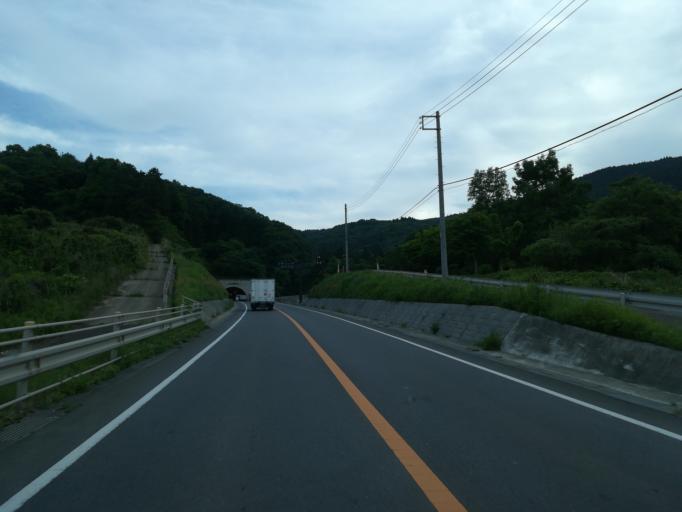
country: JP
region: Ibaraki
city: Tsukuba
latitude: 36.1830
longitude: 140.1672
